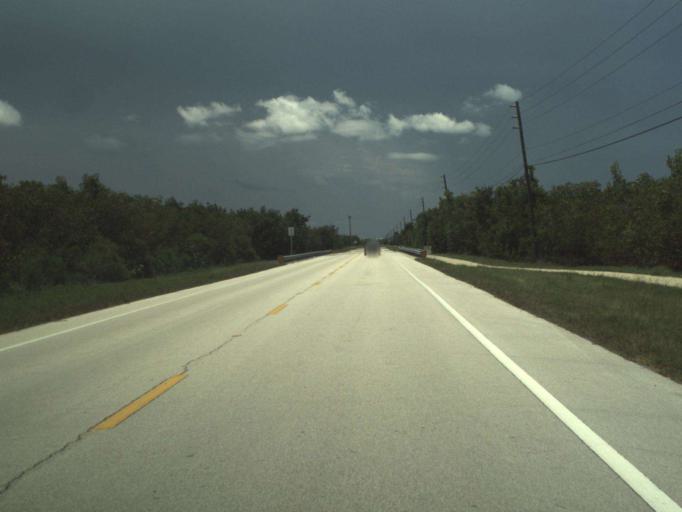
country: US
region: Florida
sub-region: Saint Lucie County
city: Fort Pierce
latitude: 27.4141
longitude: -80.2740
